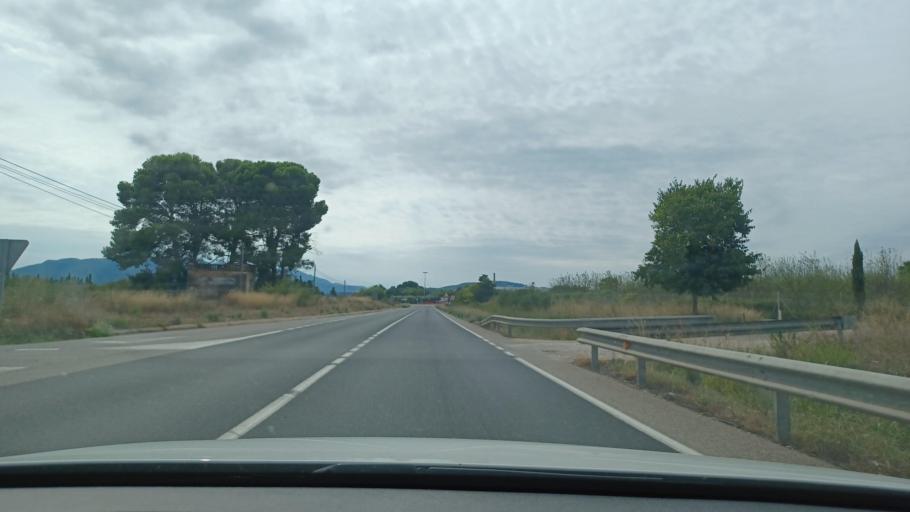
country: ES
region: Catalonia
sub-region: Provincia de Tarragona
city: Santa Barbara
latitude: 40.7262
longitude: 0.5032
